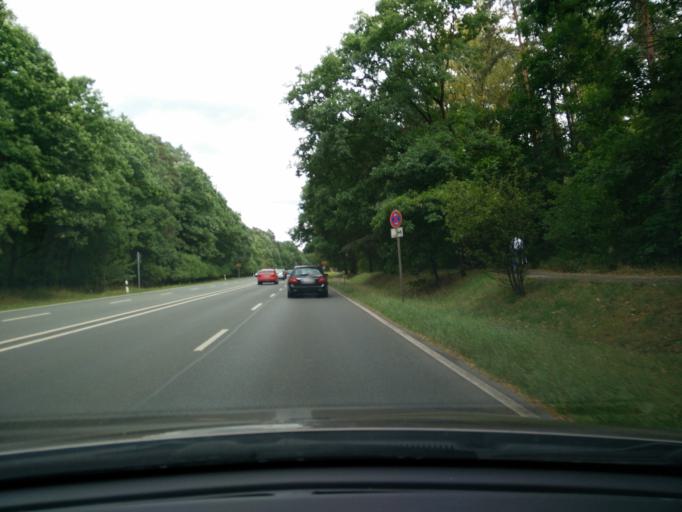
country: DE
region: Bavaria
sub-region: Regierungsbezirk Mittelfranken
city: Nuernberg
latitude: 49.4304
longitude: 11.1371
